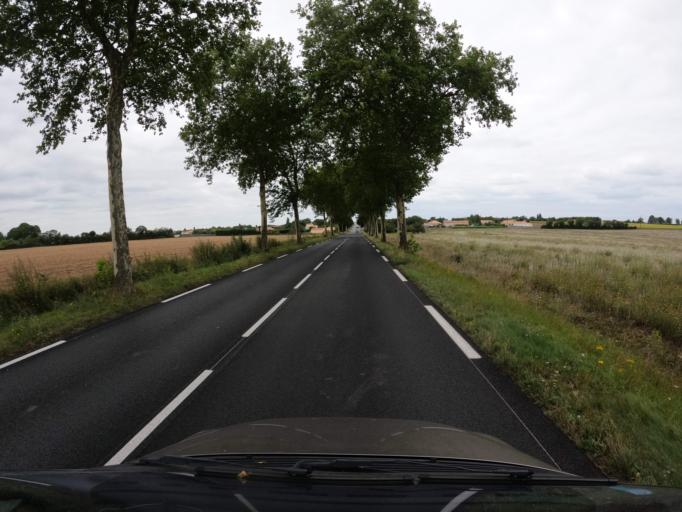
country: FR
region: Pays de la Loire
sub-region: Departement de la Vendee
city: Le Langon
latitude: 46.5035
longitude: -0.9399
